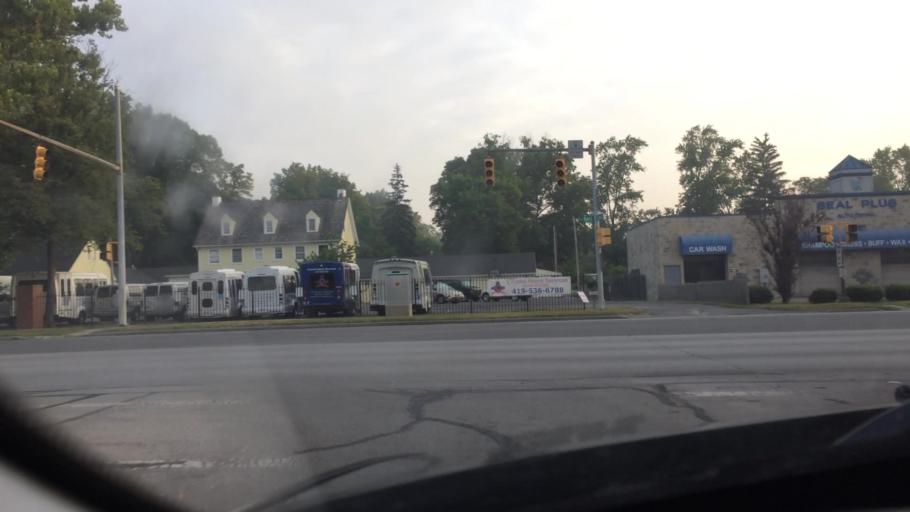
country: US
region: Ohio
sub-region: Lucas County
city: Ottawa Hills
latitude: 41.6530
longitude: -83.6571
